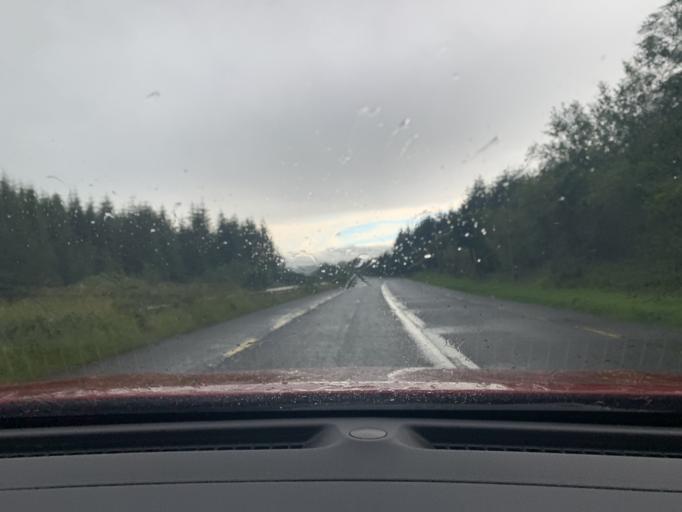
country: IE
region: Ulster
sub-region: County Donegal
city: Letterkenny
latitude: 54.8842
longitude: -7.7375
